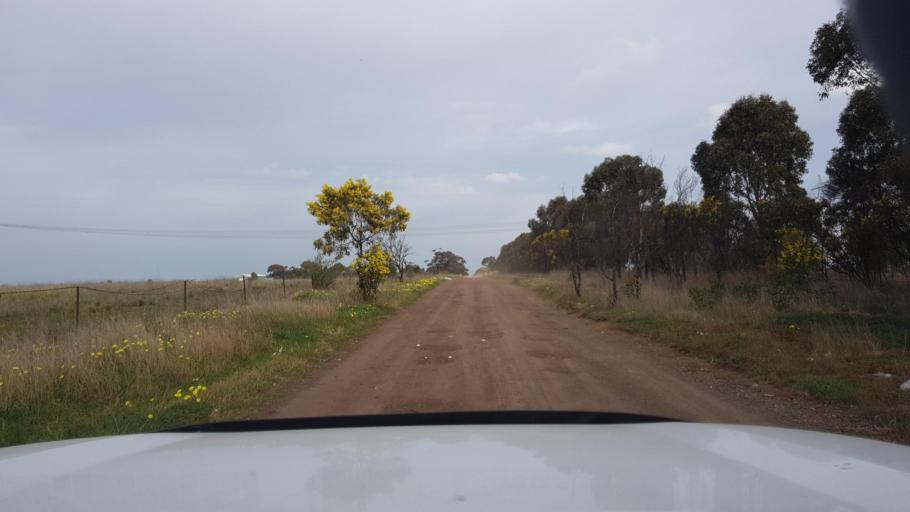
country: AU
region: Victoria
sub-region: Melton
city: Rockbank
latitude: -37.7716
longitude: 144.6453
